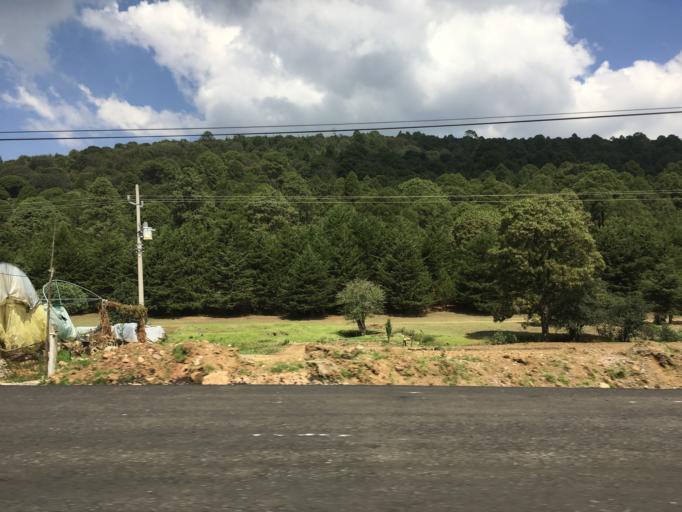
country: MX
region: Mexico
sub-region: Morelos
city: San Marcos Tlazalpan
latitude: 19.8388
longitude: -99.7033
